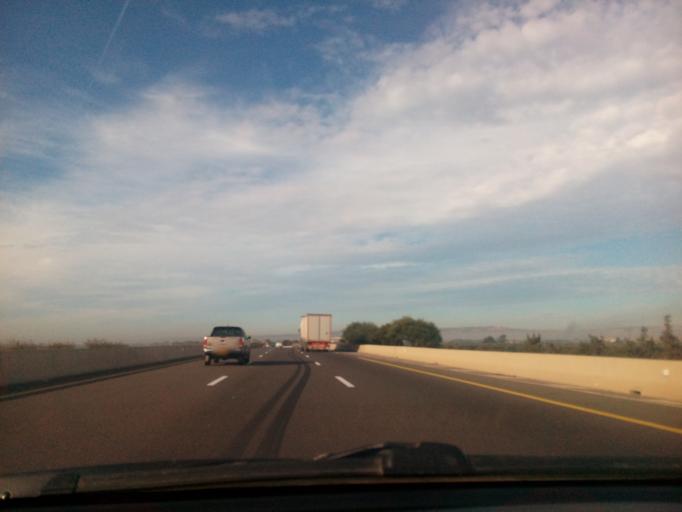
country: DZ
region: Mascara
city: Sig
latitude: 35.5842
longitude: -0.2011
